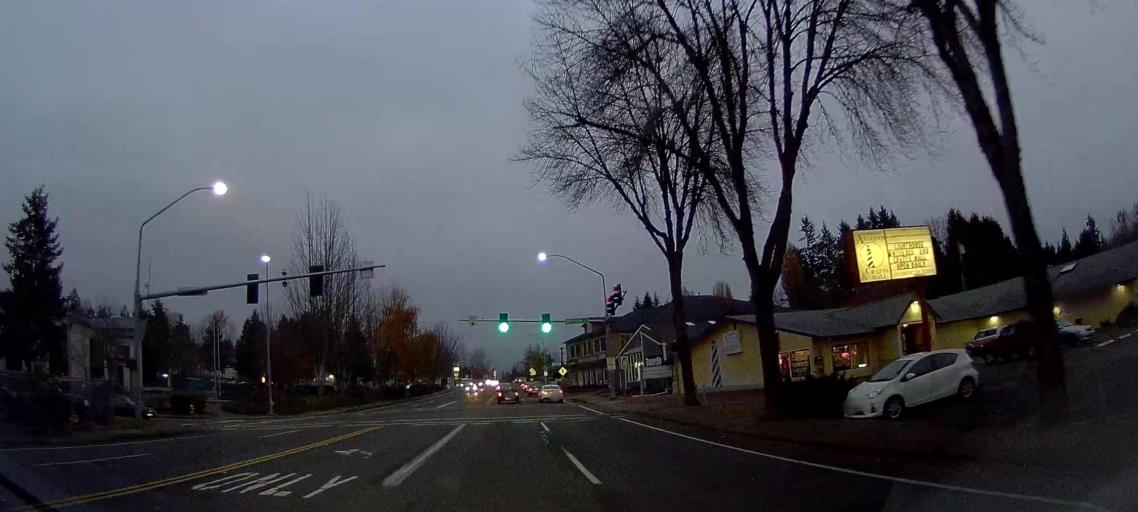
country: US
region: Washington
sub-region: Thurston County
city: Lacey
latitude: 47.0431
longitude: -122.8595
